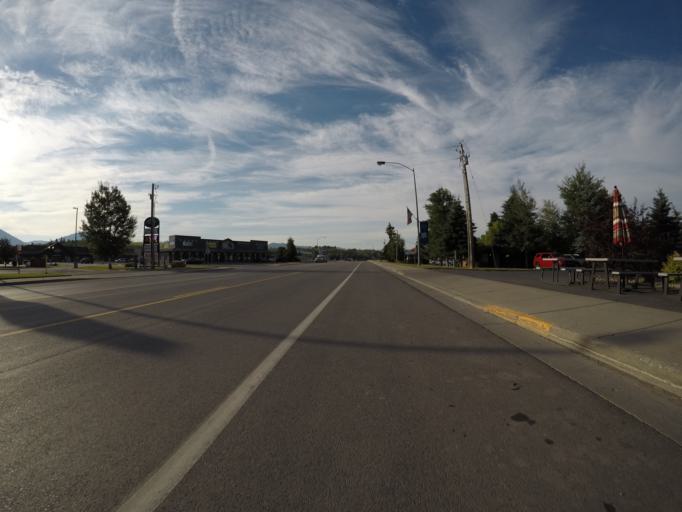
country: US
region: Wyoming
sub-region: Lincoln County
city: Afton
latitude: 42.9155
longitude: -111.0015
